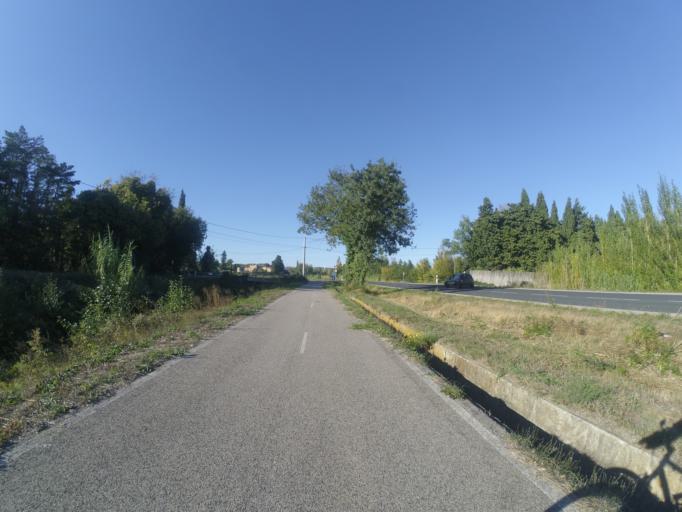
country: FR
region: Languedoc-Roussillon
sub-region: Departement des Pyrenees-Orientales
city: Pezilla-la-Riviere
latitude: 42.6877
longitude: 2.7525
